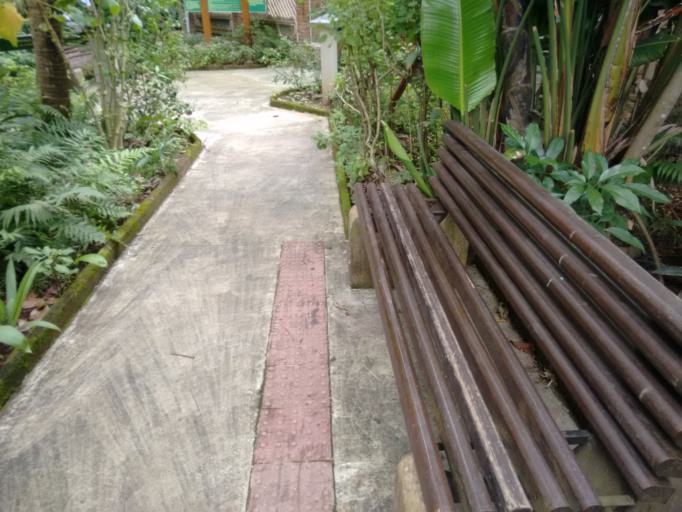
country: BR
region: Sao Paulo
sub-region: Santos
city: Santos
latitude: -23.9661
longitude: -46.3499
